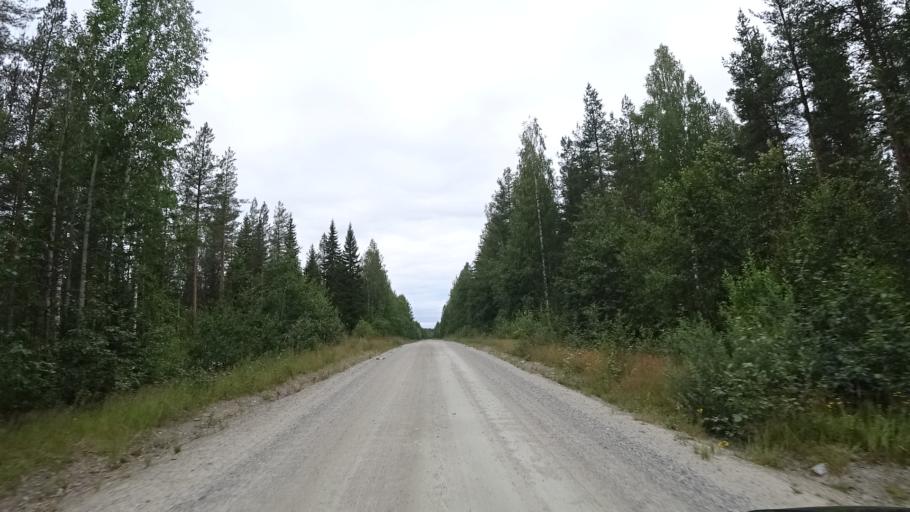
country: FI
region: North Karelia
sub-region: Joensuu
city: Eno
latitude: 63.1552
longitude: 30.6062
